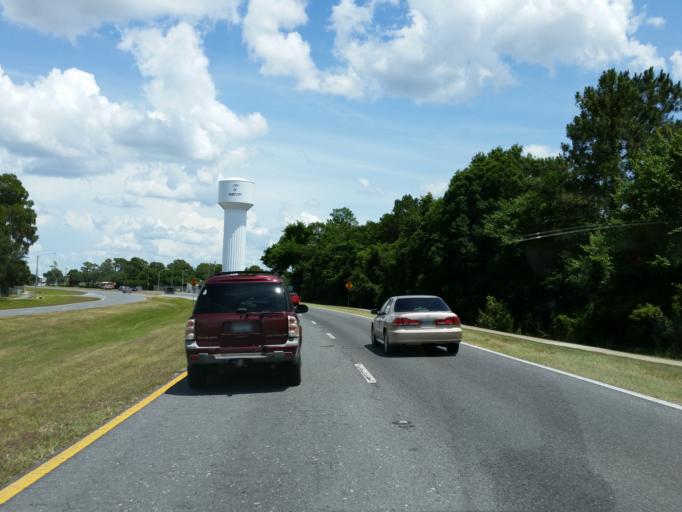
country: US
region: Florida
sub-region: Hillsborough County
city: Plant City
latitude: 27.9899
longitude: -82.1350
